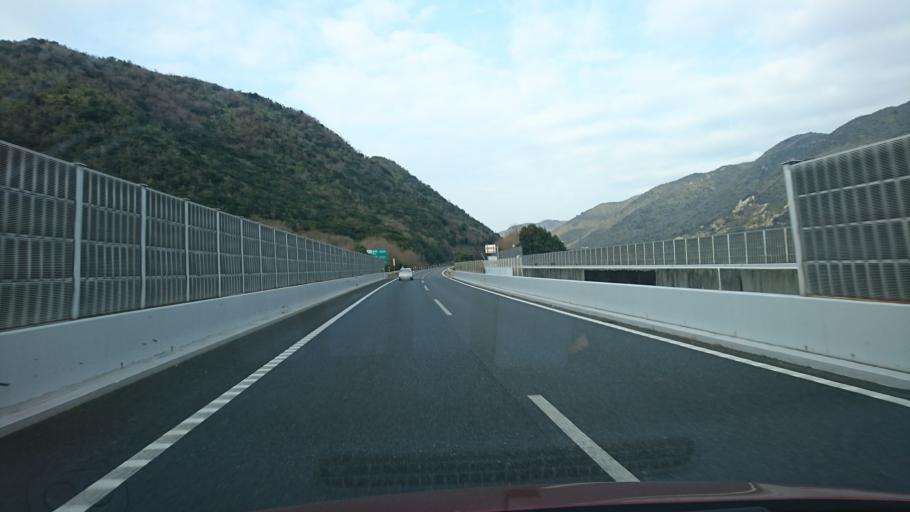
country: JP
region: Hyogo
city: Kariya
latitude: 34.7737
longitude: 134.3653
